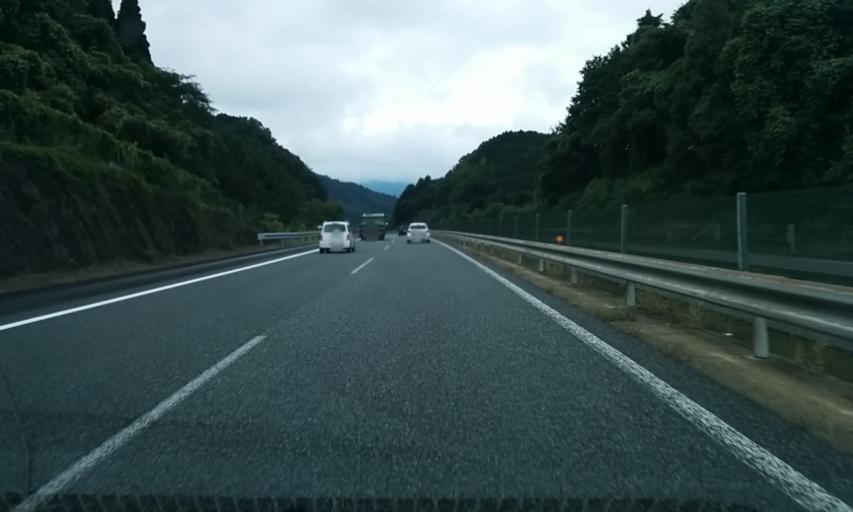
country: JP
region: Kyoto
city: Fukuchiyama
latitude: 35.1958
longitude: 135.1474
